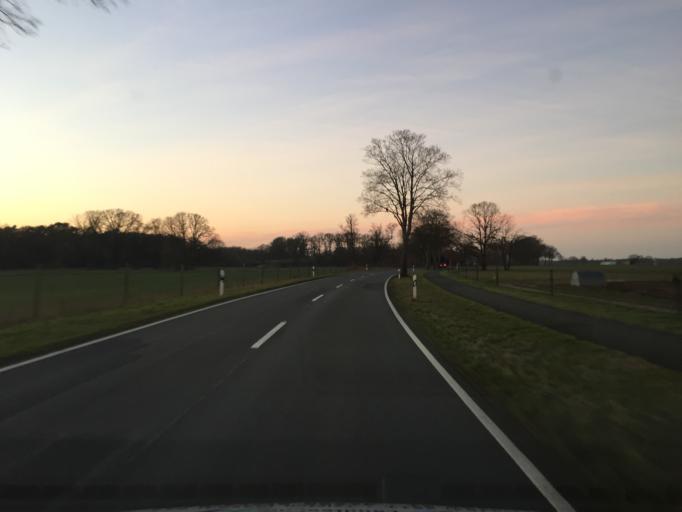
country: DE
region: Lower Saxony
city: Borstel
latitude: 52.6019
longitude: 8.9420
